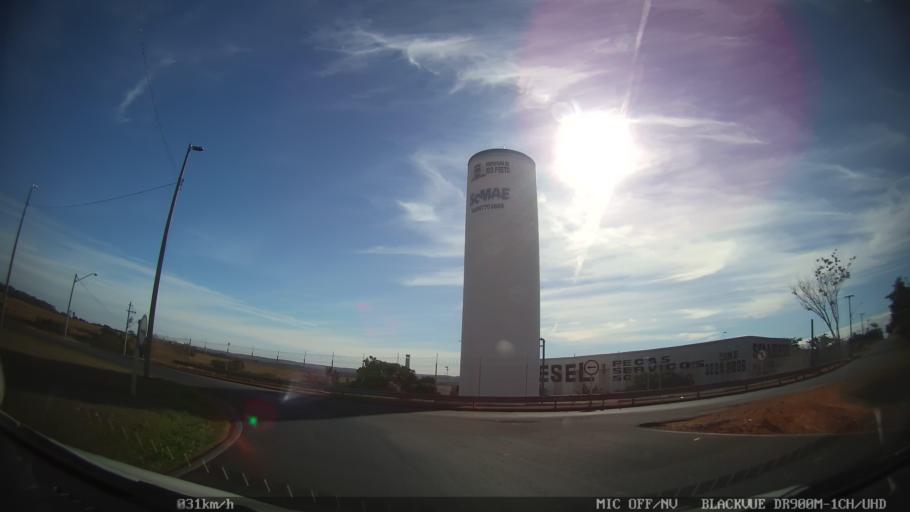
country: BR
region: Sao Paulo
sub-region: Sao Jose Do Rio Preto
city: Sao Jose do Rio Preto
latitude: -20.7349
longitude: -49.3384
